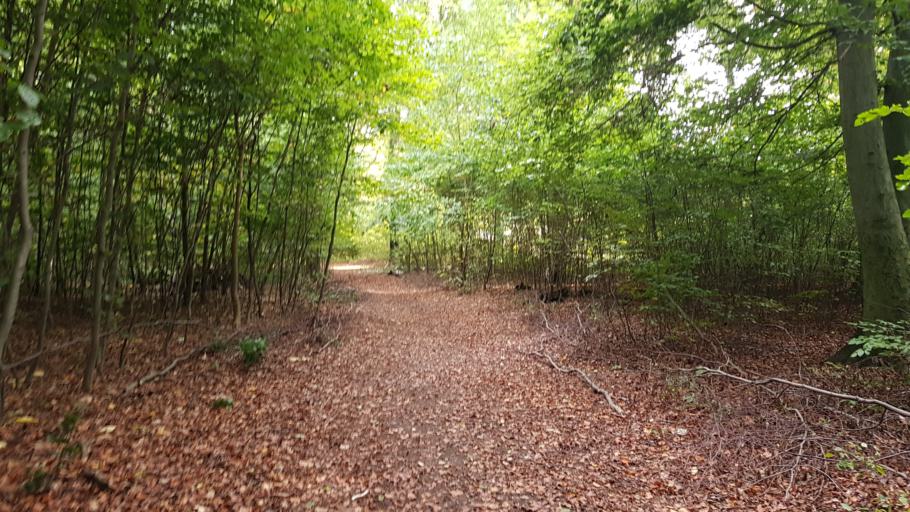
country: DE
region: Berlin
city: Baumschulenweg
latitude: 52.4773
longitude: 13.4913
